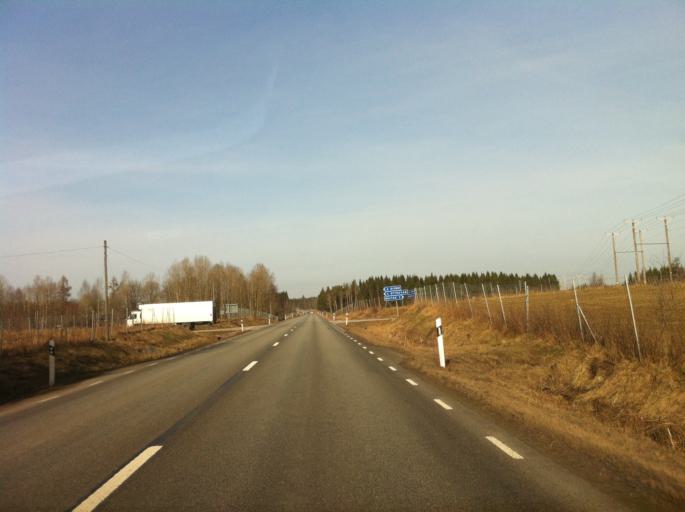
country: SE
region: Vaestra Goetaland
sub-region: Tidaholms Kommun
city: Tidaholm
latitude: 58.1616
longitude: 13.9046
